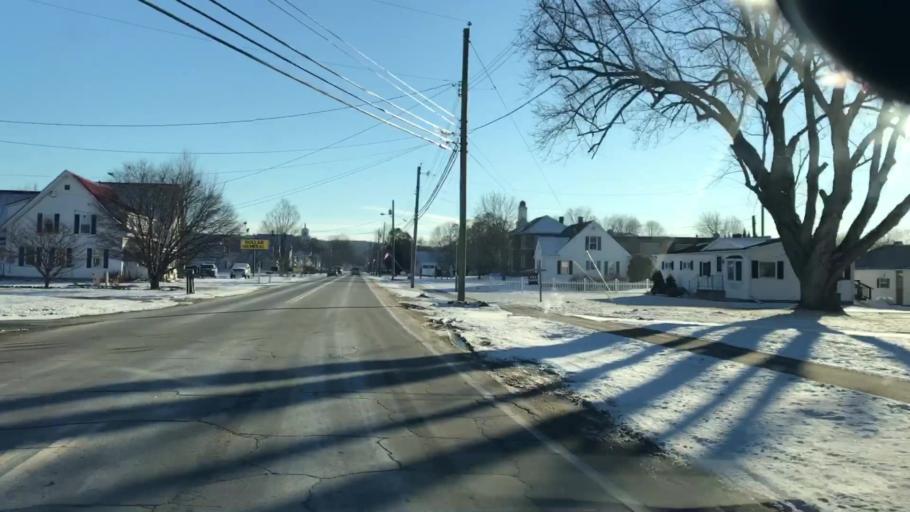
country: US
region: New Hampshire
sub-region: Grafton County
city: North Haverhill
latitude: 44.0973
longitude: -72.0250
